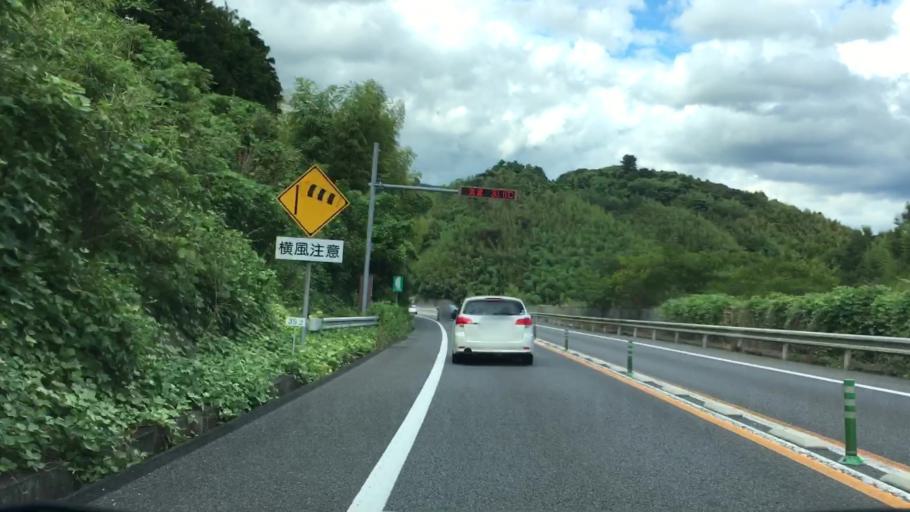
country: JP
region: Saga Prefecture
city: Karatsu
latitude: 33.4286
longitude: 130.0466
